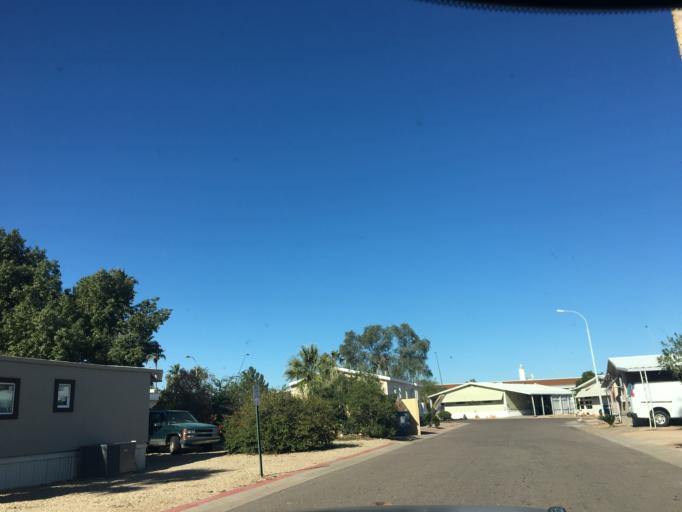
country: US
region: Arizona
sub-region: Maricopa County
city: Mesa
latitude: 33.4503
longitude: -111.8433
